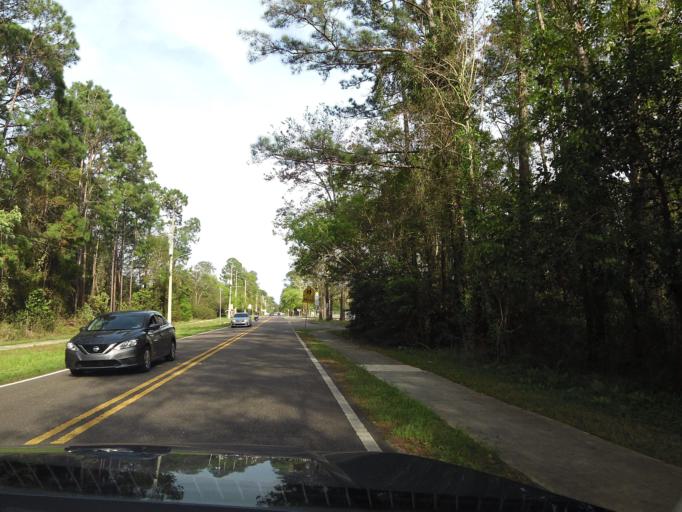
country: US
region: Florida
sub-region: Clay County
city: Bellair-Meadowbrook Terrace
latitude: 30.2262
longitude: -81.7420
